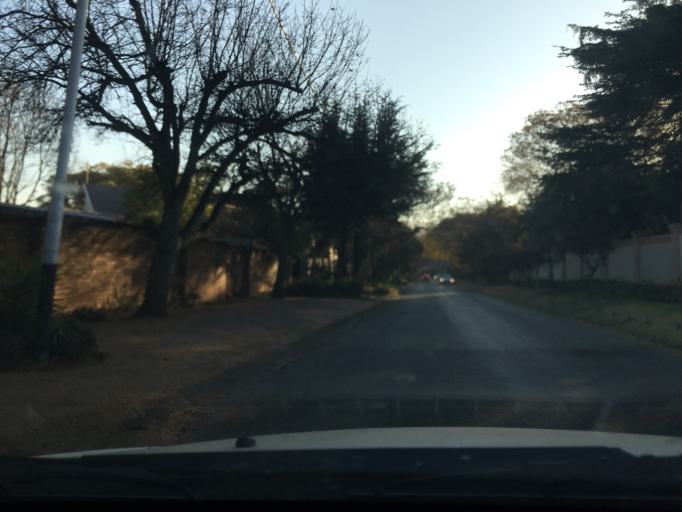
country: ZA
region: Gauteng
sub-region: City of Johannesburg Metropolitan Municipality
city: Johannesburg
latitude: -26.0724
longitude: 28.0165
